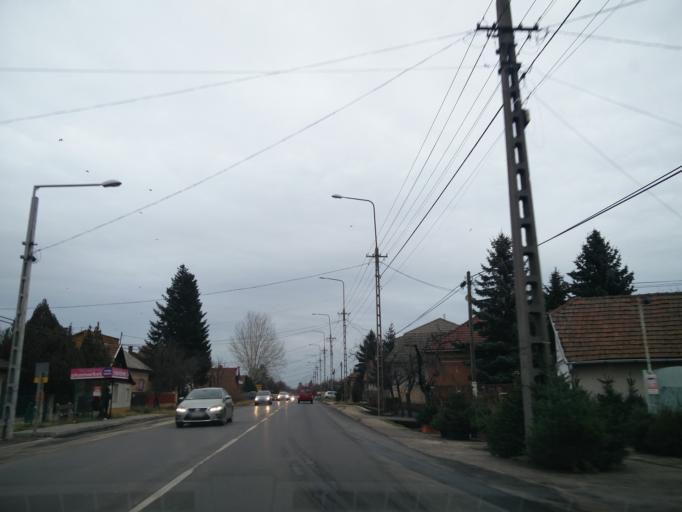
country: HU
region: Pest
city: Ullo
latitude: 47.3888
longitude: 19.3290
